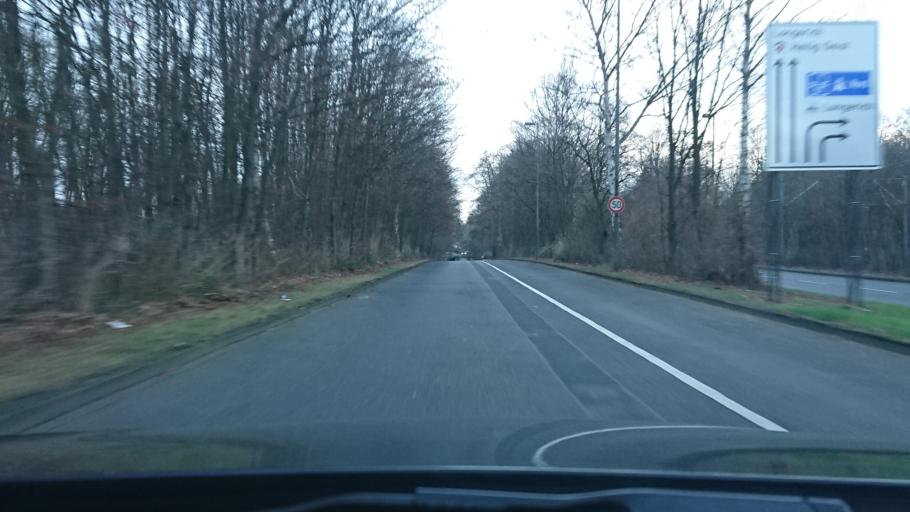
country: DE
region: North Rhine-Westphalia
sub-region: Regierungsbezirk Koln
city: Bilderstoeckchen
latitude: 51.0031
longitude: 6.9132
